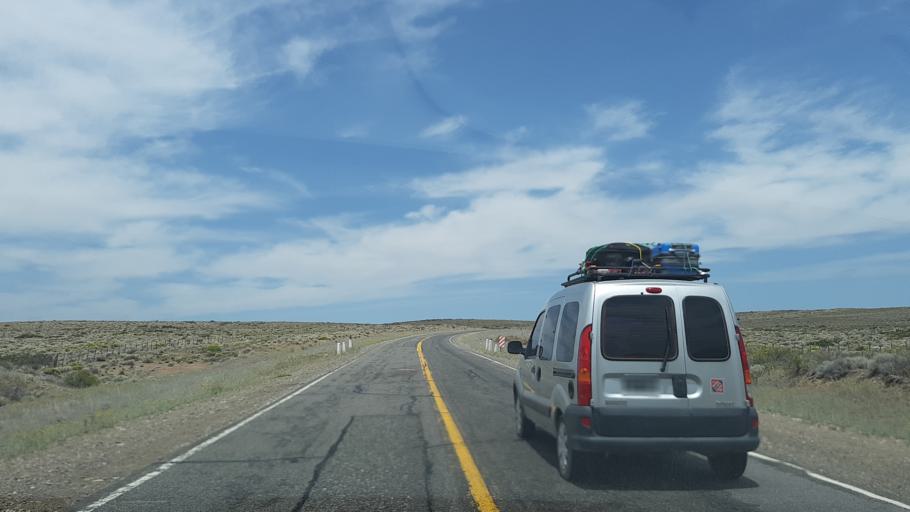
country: AR
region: Rio Negro
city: Pilcaniyeu
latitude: -40.4923
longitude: -70.6788
